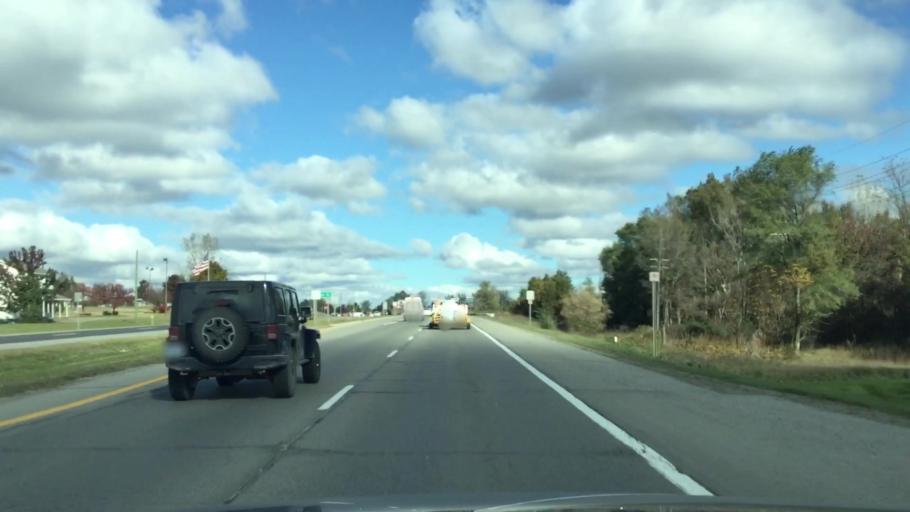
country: US
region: Michigan
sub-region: Oakland County
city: Lake Orion
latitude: 42.8007
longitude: -83.2472
